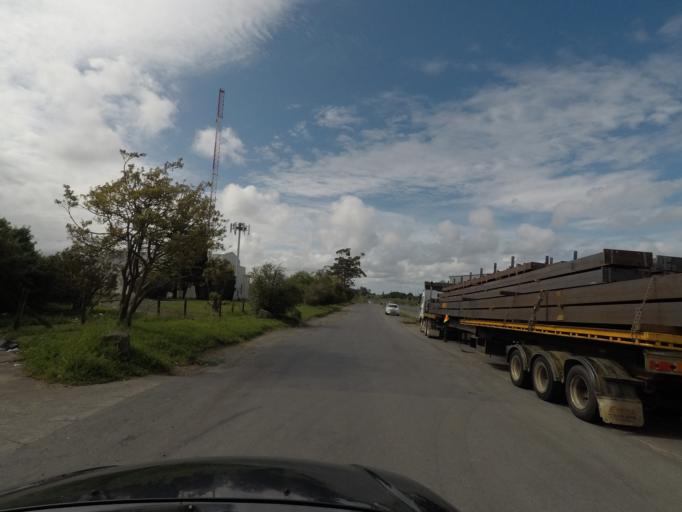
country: NZ
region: Auckland
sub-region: Auckland
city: Rosebank
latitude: -36.8461
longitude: 174.6314
